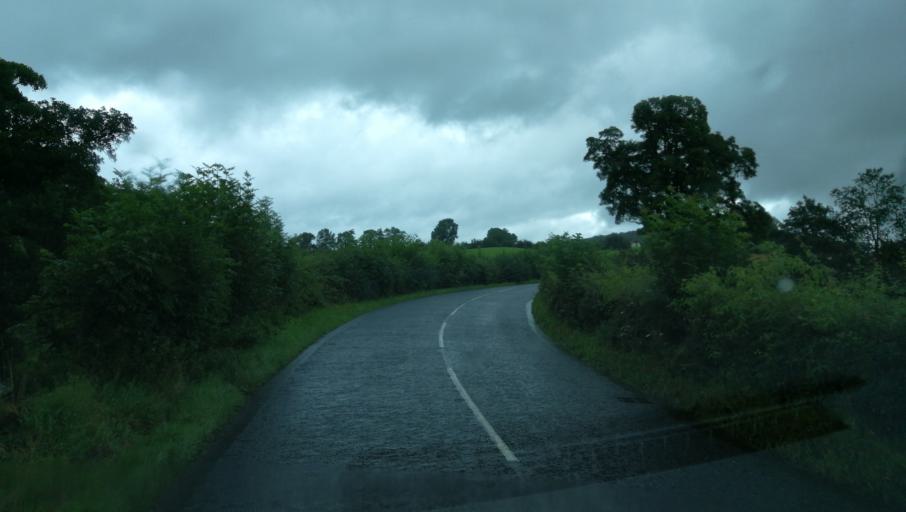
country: GB
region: England
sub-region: Cumbria
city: Penrith
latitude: 54.5973
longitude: -2.8600
